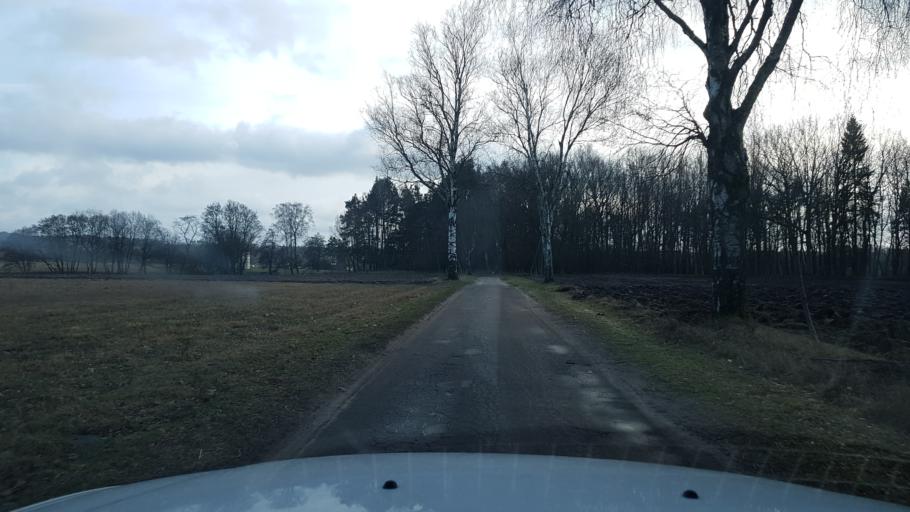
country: PL
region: West Pomeranian Voivodeship
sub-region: Powiat szczecinecki
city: Borne Sulinowo
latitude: 53.6256
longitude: 16.6134
